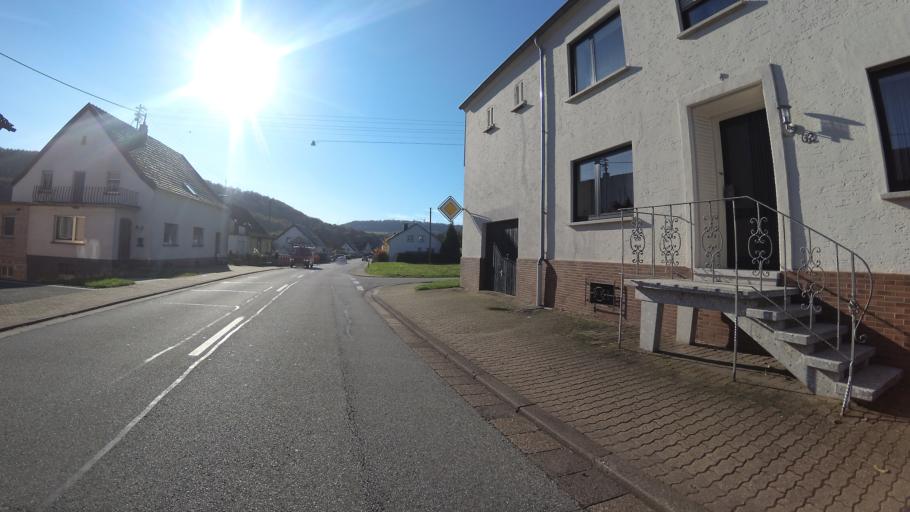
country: DE
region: Saarland
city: Losheim
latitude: 49.4623
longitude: 6.7506
